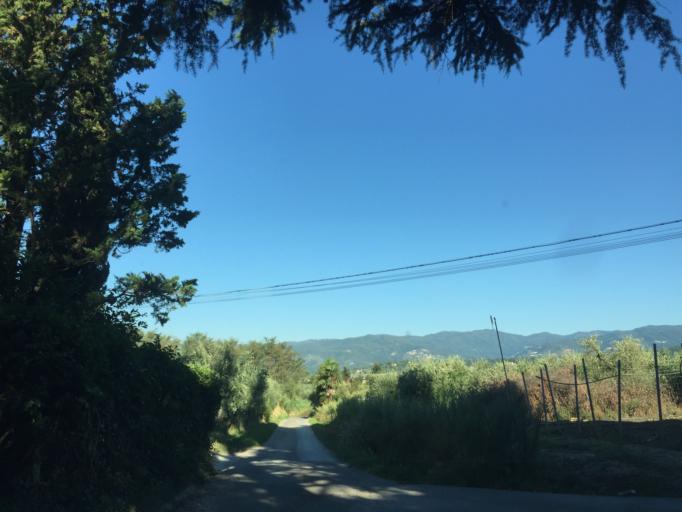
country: IT
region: Tuscany
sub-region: Provincia di Pistoia
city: Pistoia
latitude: 43.9481
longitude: 10.9479
